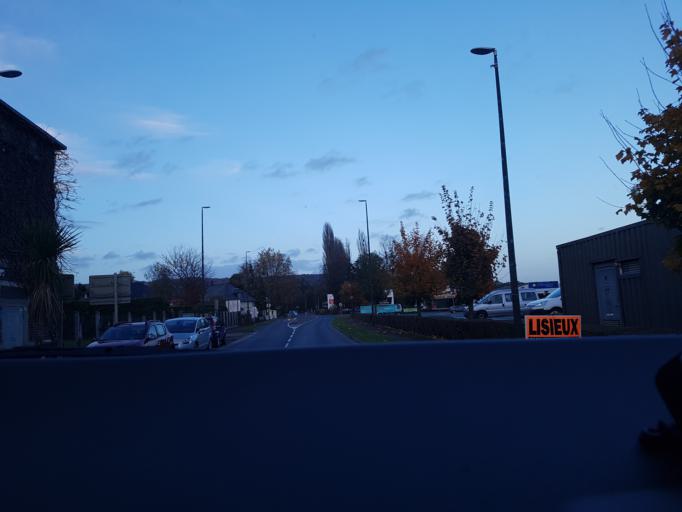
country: FR
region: Lower Normandy
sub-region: Departement du Calvados
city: Saint-Gatien-des-Bois
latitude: 49.2917
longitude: 0.1926
